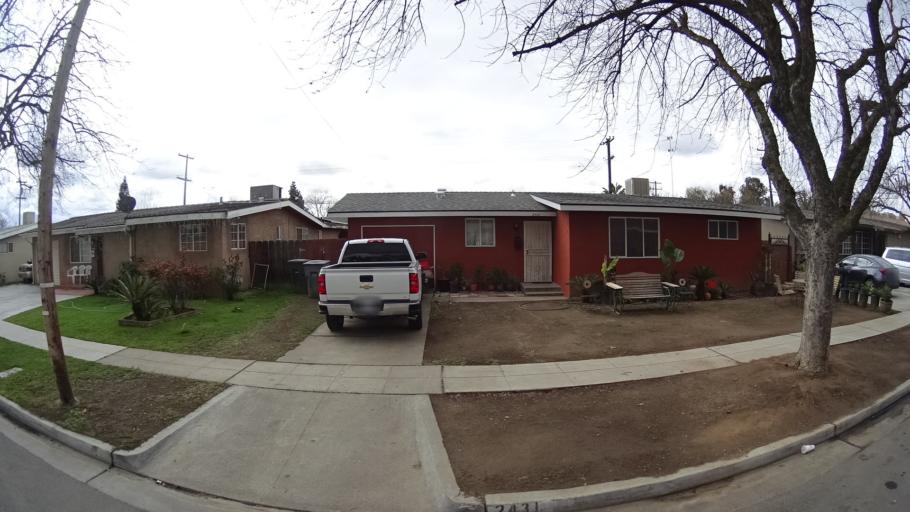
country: US
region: California
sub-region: Fresno County
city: West Park
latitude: 36.7822
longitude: -119.8397
